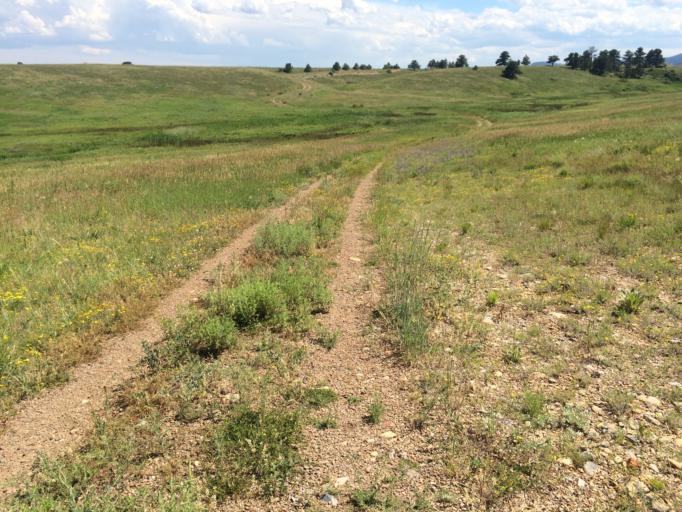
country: US
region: Colorado
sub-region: Boulder County
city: Superior
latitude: 39.8988
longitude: -105.2219
